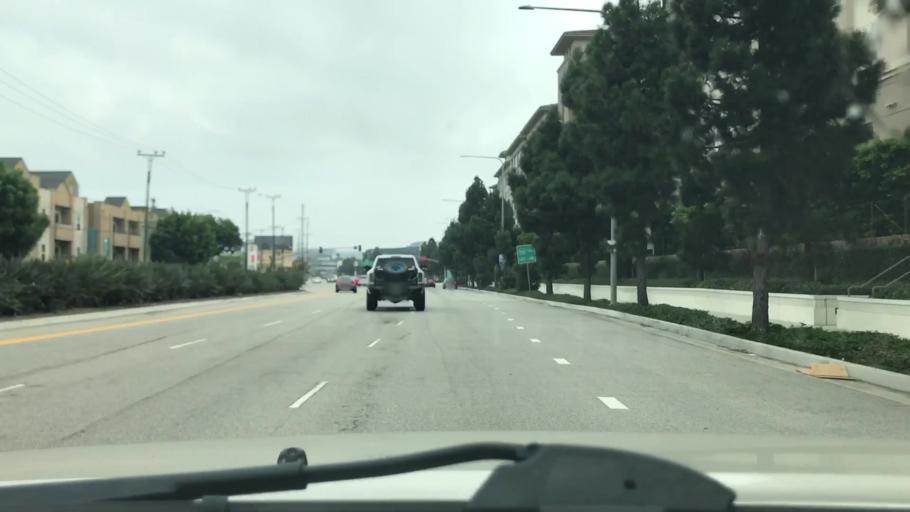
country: US
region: California
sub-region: Los Angeles County
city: Ladera Heights
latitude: 33.9804
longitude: -118.4109
